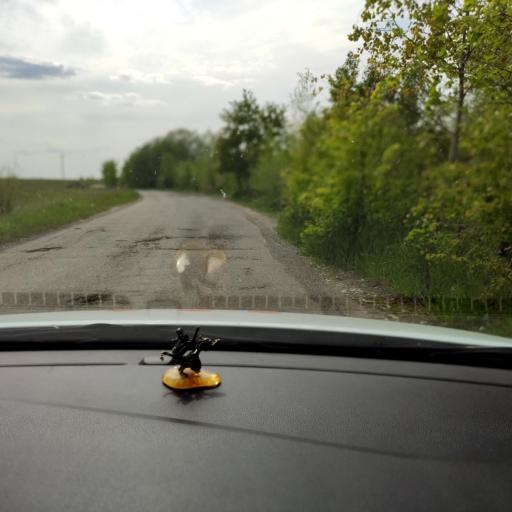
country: RU
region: Tatarstan
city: Verkhniy Uslon
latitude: 55.6980
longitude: 49.0597
